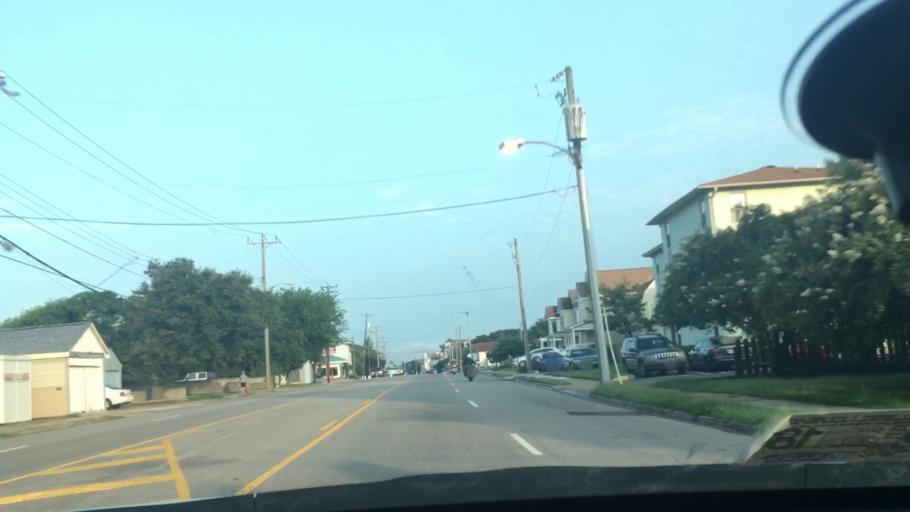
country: US
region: Virginia
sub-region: City of Norfolk
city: Norfolk
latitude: 36.9441
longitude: -76.2355
